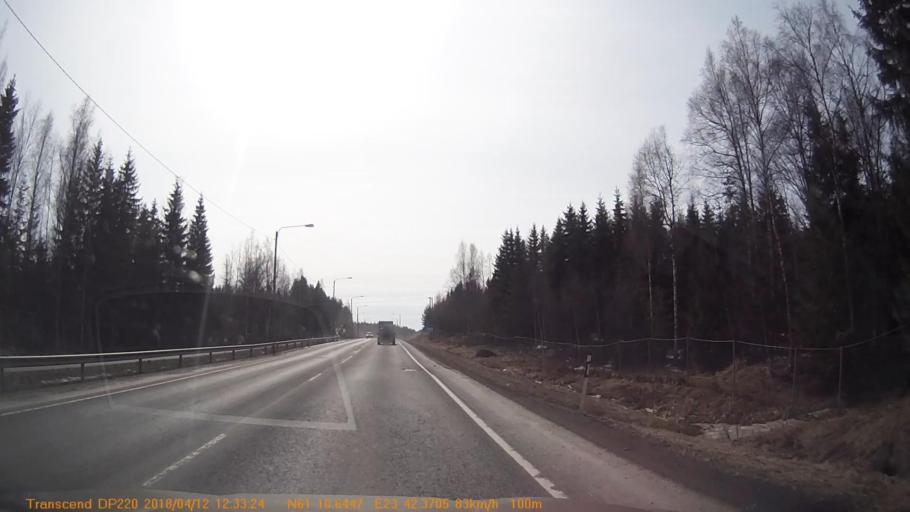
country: FI
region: Pirkanmaa
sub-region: Etelae-Pirkanmaa
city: Kylmaekoski
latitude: 61.1770
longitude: 23.7060
